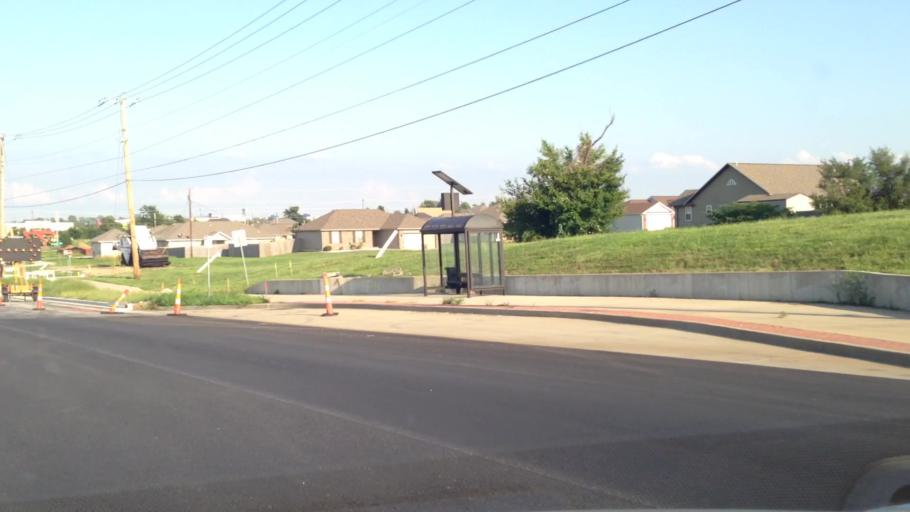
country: US
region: Missouri
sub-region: Jasper County
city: Duquesne
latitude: 37.0693
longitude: -94.4844
